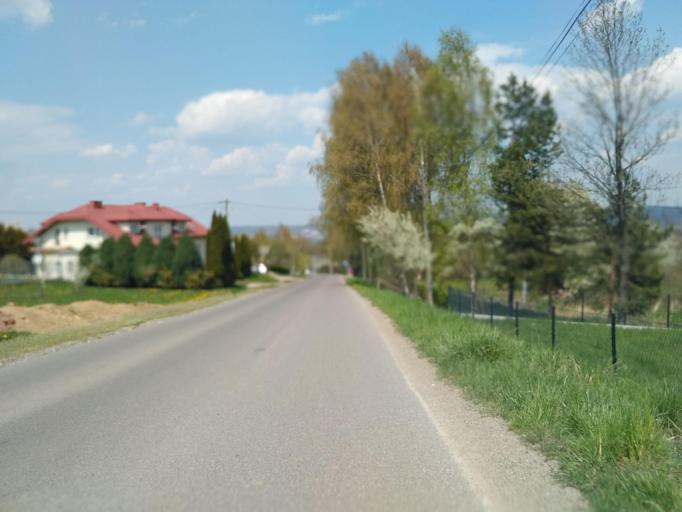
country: PL
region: Subcarpathian Voivodeship
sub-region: Powiat jasielski
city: Jaslo
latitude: 49.7130
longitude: 21.5066
